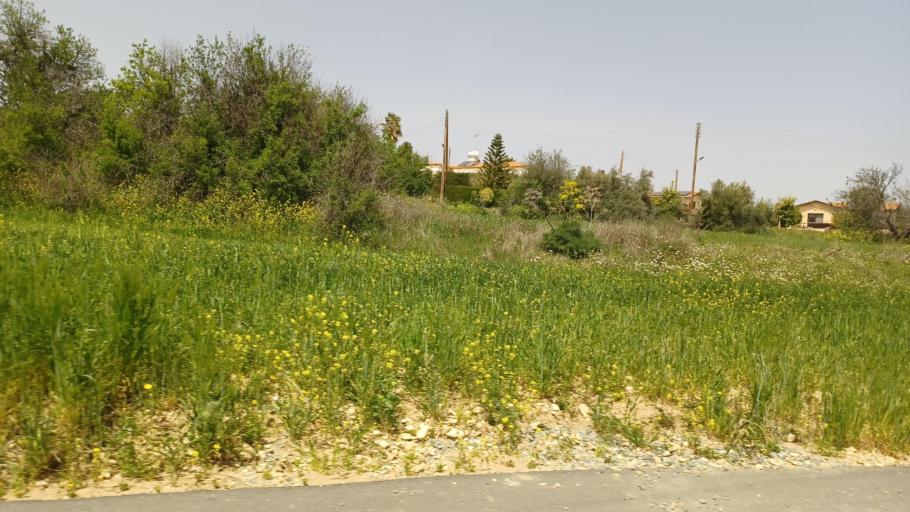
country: CY
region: Limassol
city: Pachna
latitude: 34.7368
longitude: 32.7378
